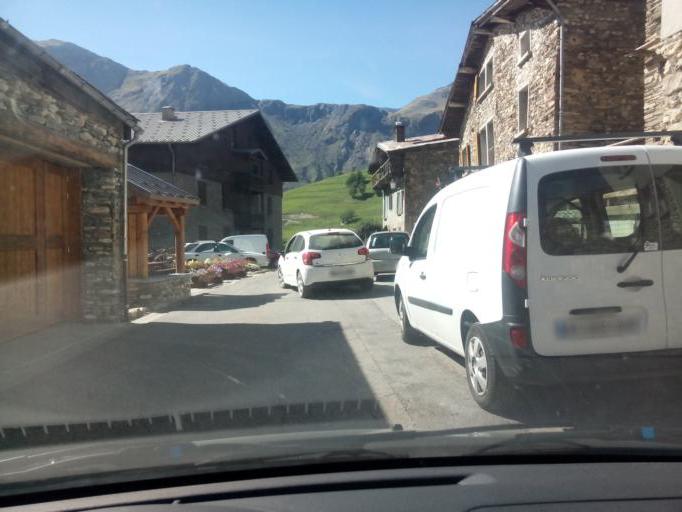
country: FR
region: Rhone-Alpes
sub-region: Departement de l'Isere
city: Mont-de-Lans
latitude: 45.0720
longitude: 6.1698
